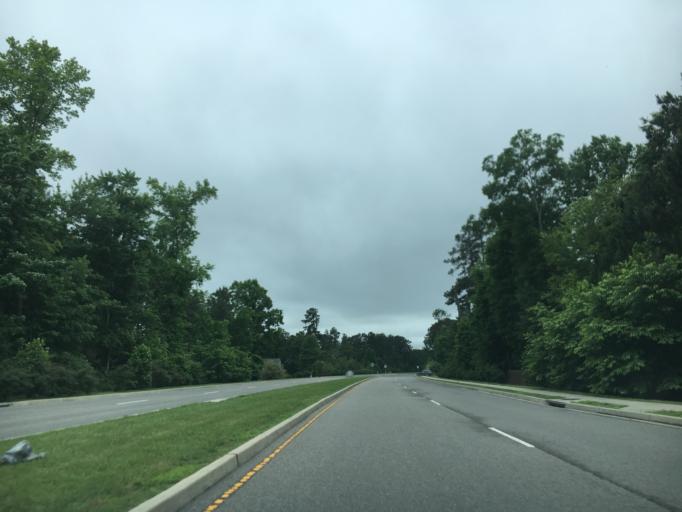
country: US
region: Virginia
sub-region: Henrico County
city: Short Pump
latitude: 37.6288
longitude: -77.6152
